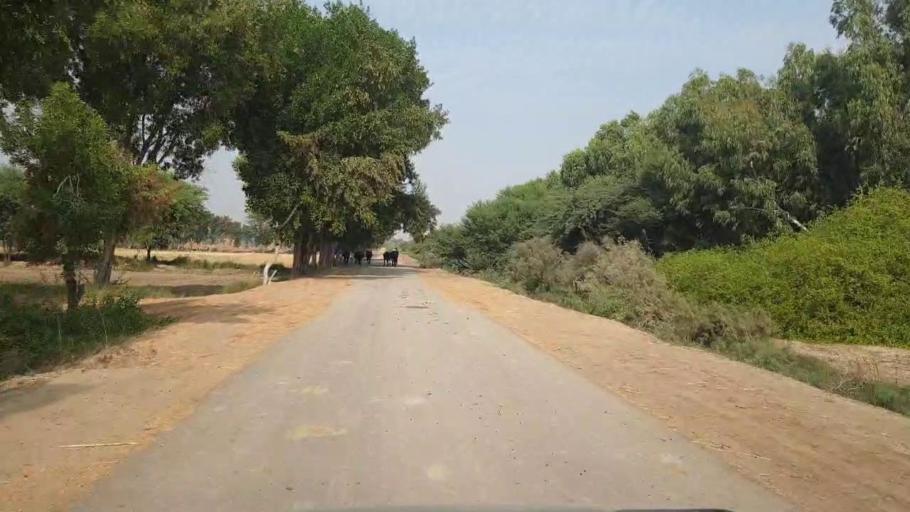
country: PK
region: Sindh
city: Tando Muhammad Khan
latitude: 25.1241
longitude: 68.4582
